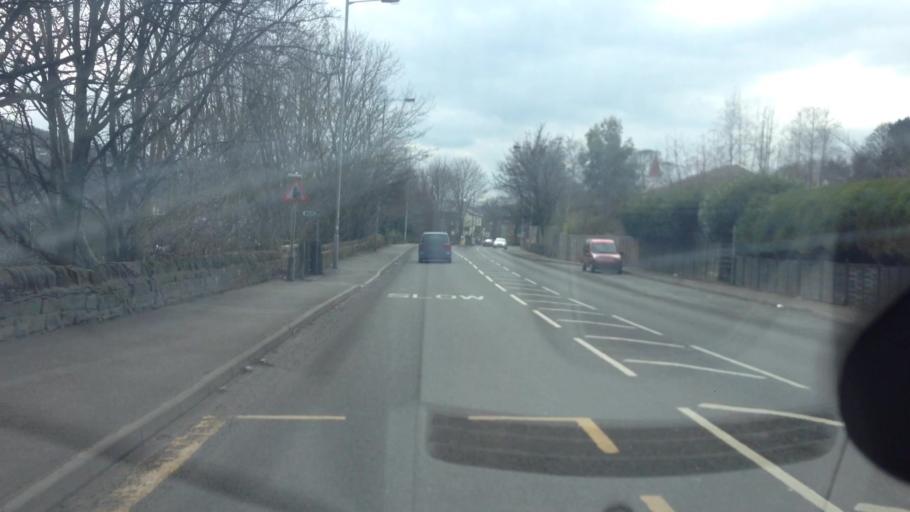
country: GB
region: England
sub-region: Bradford
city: Shipley
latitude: 53.8479
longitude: -1.7504
